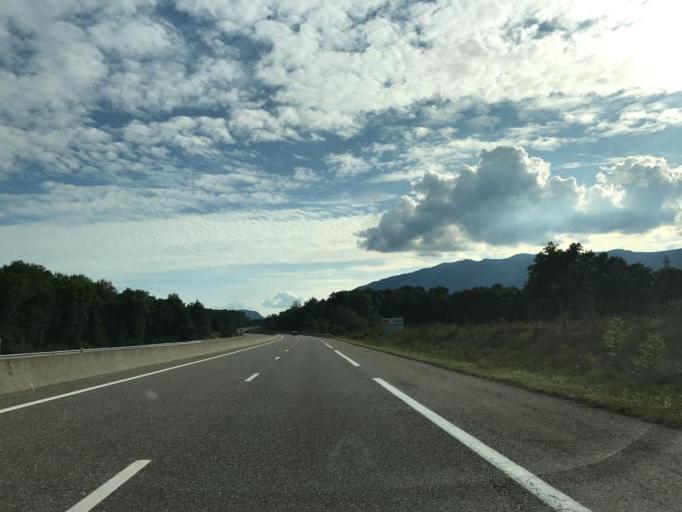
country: FR
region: Rhone-Alpes
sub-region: Departement de l'Ain
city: Challex
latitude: 46.2011
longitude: 5.9661
